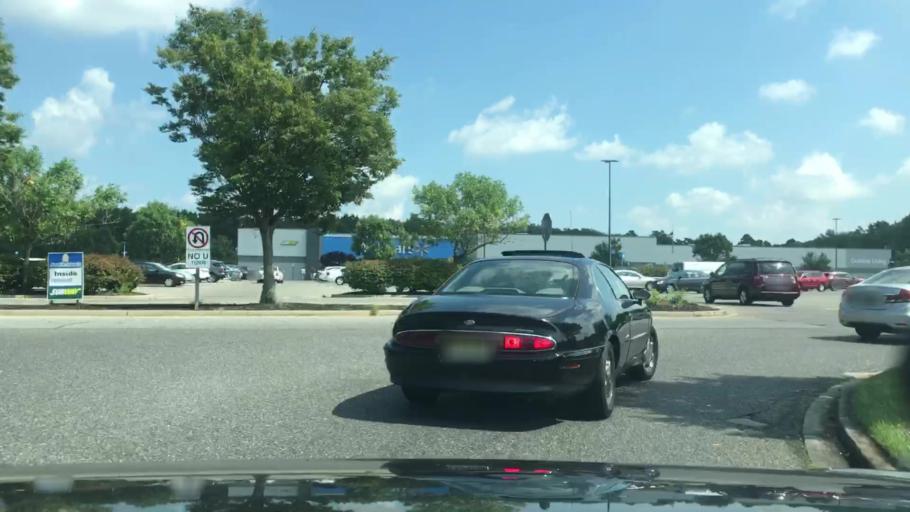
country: US
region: New Jersey
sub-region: Ocean County
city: Holiday City South
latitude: 39.9745
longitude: -74.2401
